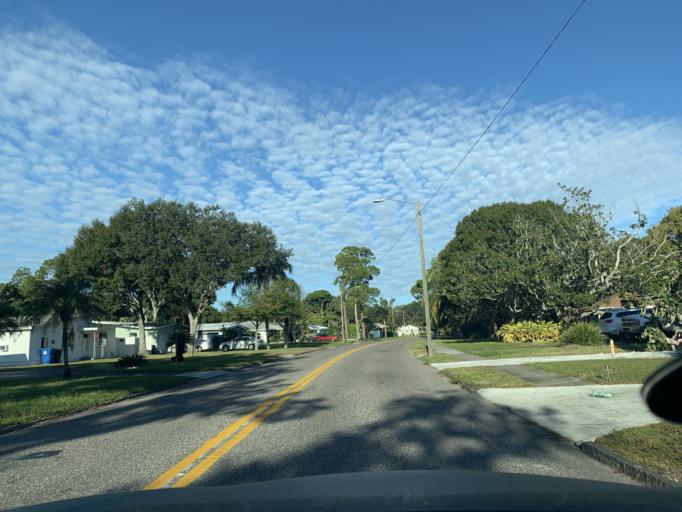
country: US
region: Florida
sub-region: Pinellas County
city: South Pasadena
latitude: 27.7635
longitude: -82.7371
